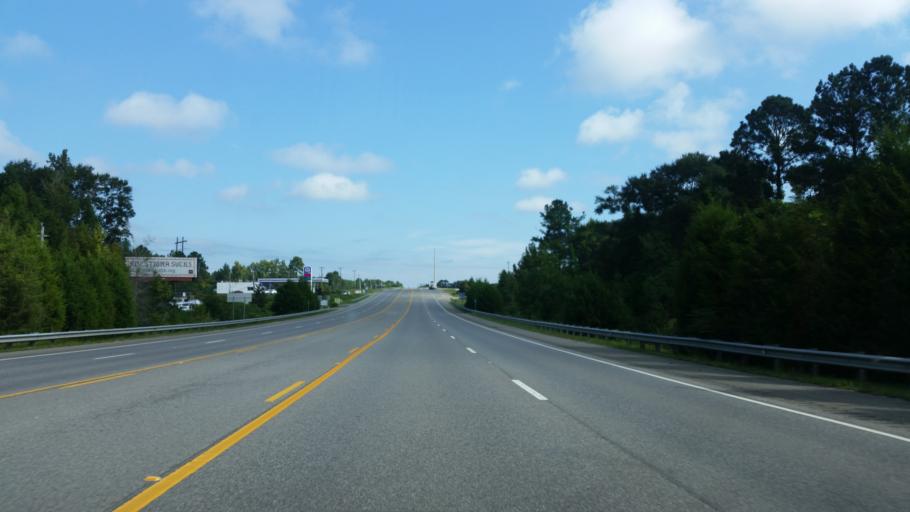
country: US
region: Alabama
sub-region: Baldwin County
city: Bay Minette
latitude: 30.9597
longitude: -87.7608
